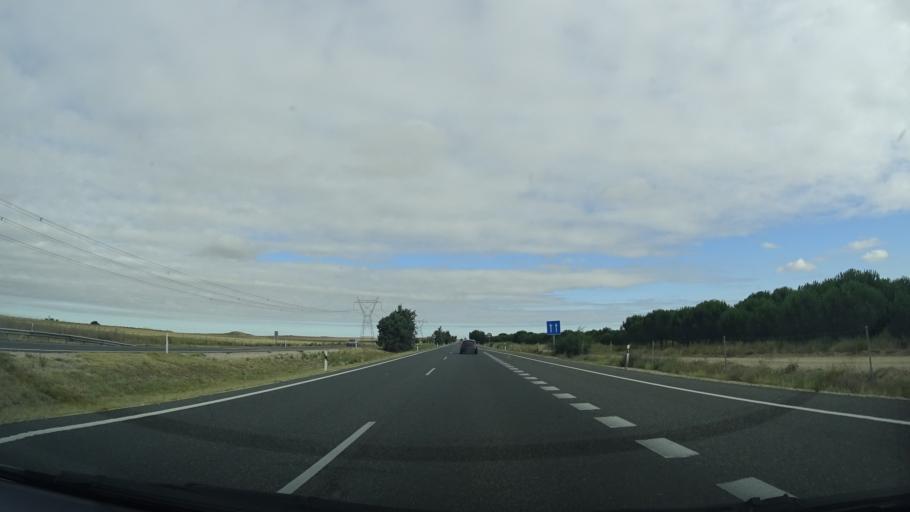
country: ES
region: Castille and Leon
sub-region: Provincia de Valladolid
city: San Pablo de la Moraleja
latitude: 41.1529
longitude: -4.7916
